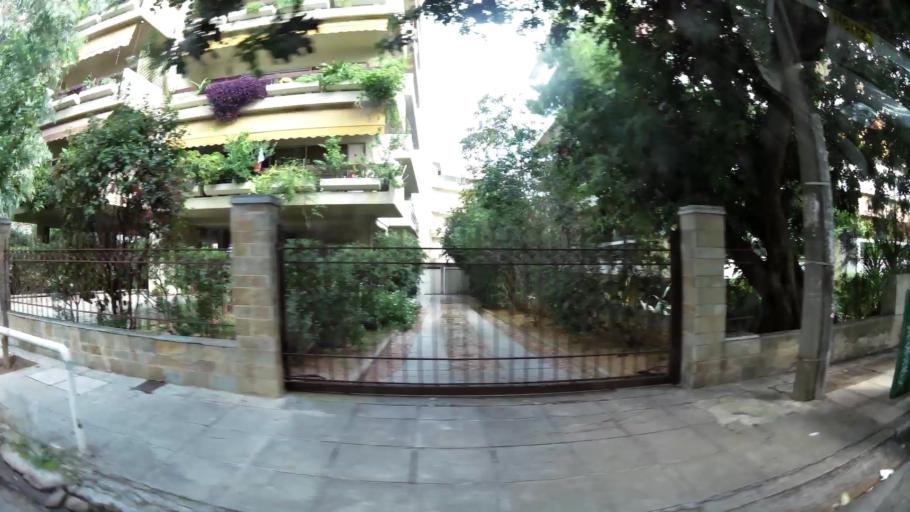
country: GR
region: Attica
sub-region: Nomarchia Athinas
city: Cholargos
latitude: 38.0017
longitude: 23.8003
